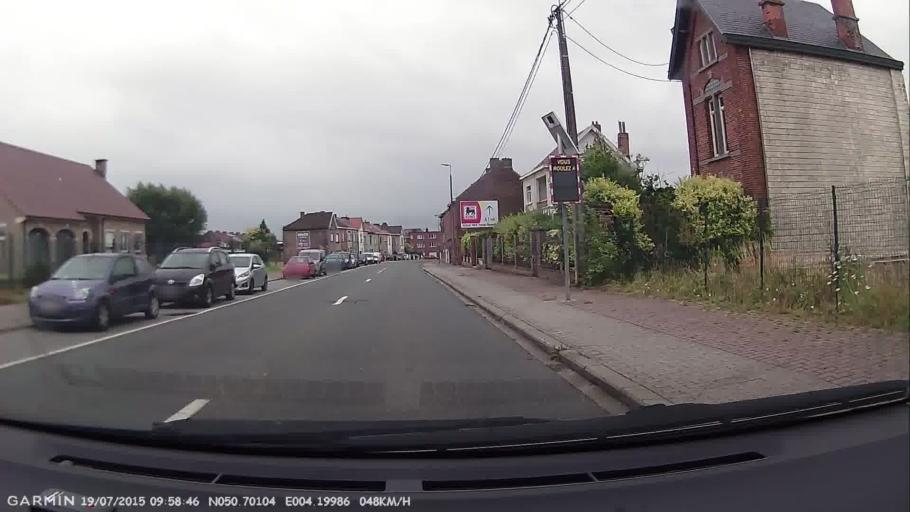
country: BE
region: Wallonia
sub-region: Province du Brabant Wallon
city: Tubize
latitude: 50.7010
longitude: 4.1999
